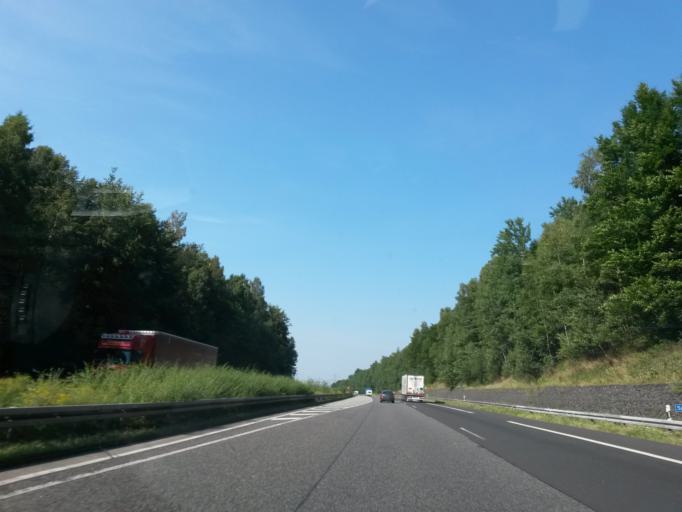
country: DE
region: Hesse
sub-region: Regierungsbezirk Kassel
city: Eichenzell
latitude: 50.5056
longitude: 9.7374
